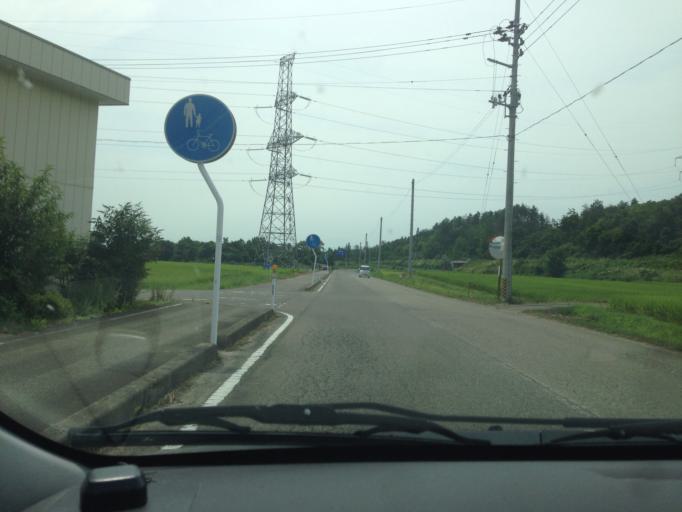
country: JP
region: Fukushima
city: Kitakata
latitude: 37.7119
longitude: 139.8695
